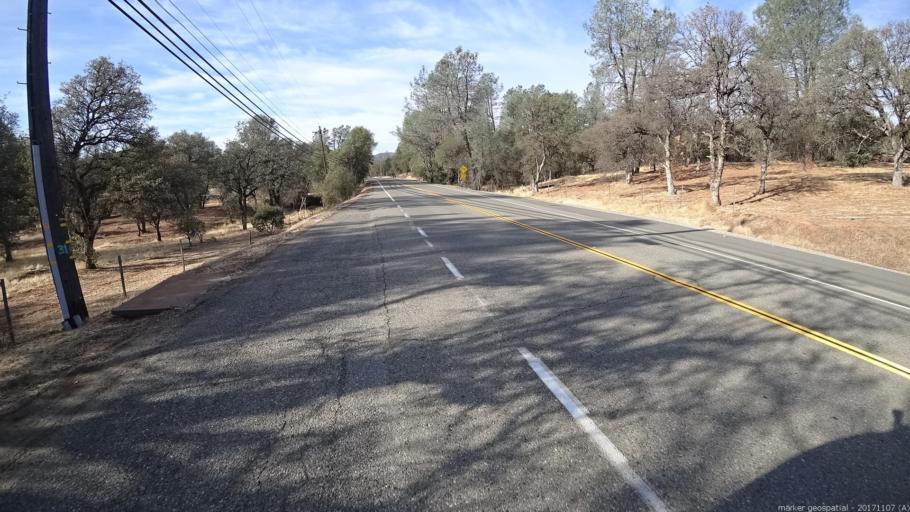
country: US
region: California
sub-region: Shasta County
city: Redding
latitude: 40.5559
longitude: -122.4397
